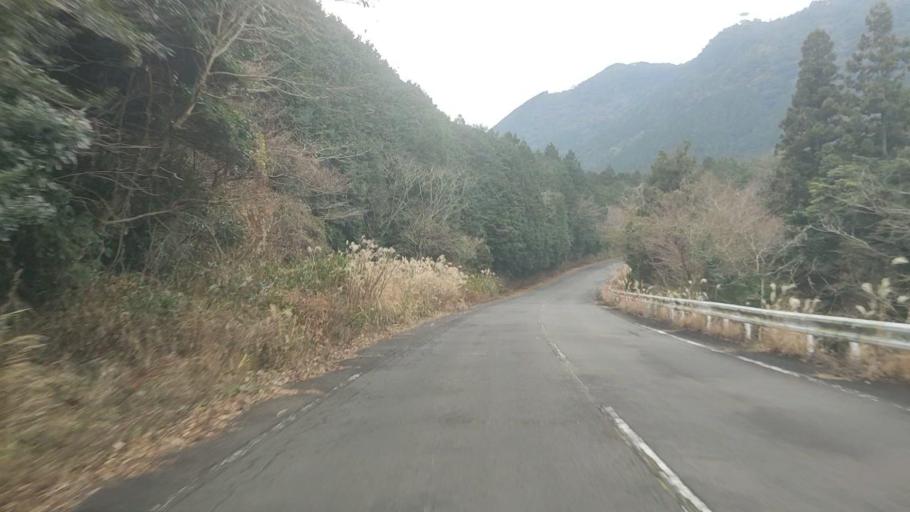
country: JP
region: Nagasaki
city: Shimabara
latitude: 32.7956
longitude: 130.2860
